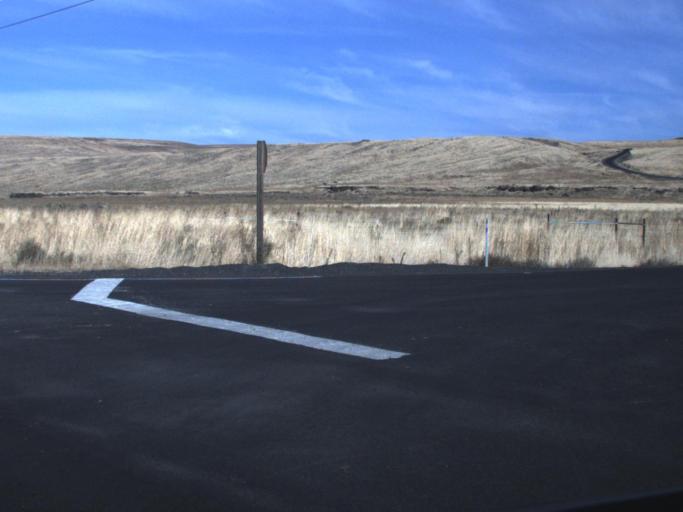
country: US
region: Washington
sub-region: Franklin County
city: Connell
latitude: 46.6478
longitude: -118.5887
